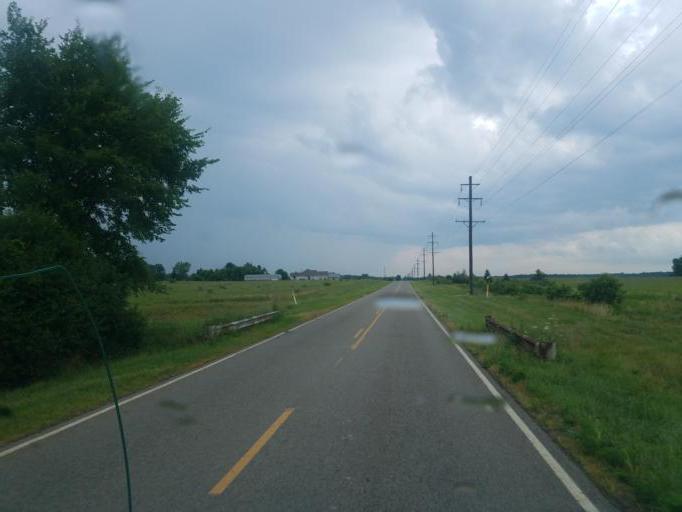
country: US
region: Ohio
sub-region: Defiance County
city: Hicksville
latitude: 41.3716
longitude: -84.7670
